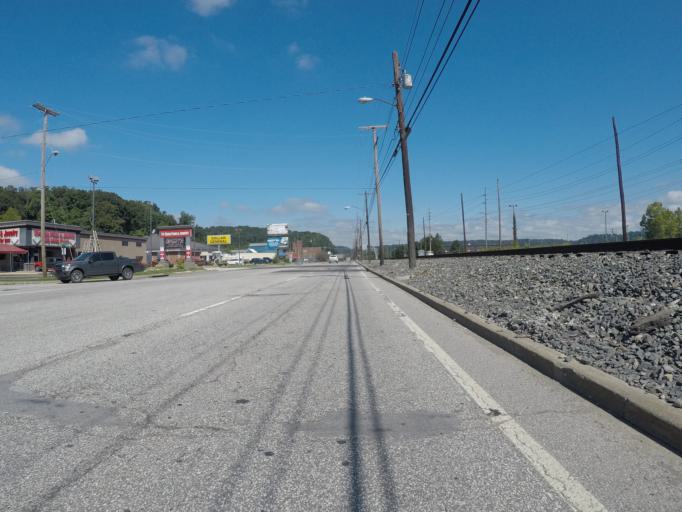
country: US
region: Kentucky
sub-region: Boyd County
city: Ashland
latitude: 38.4496
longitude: -82.6122
